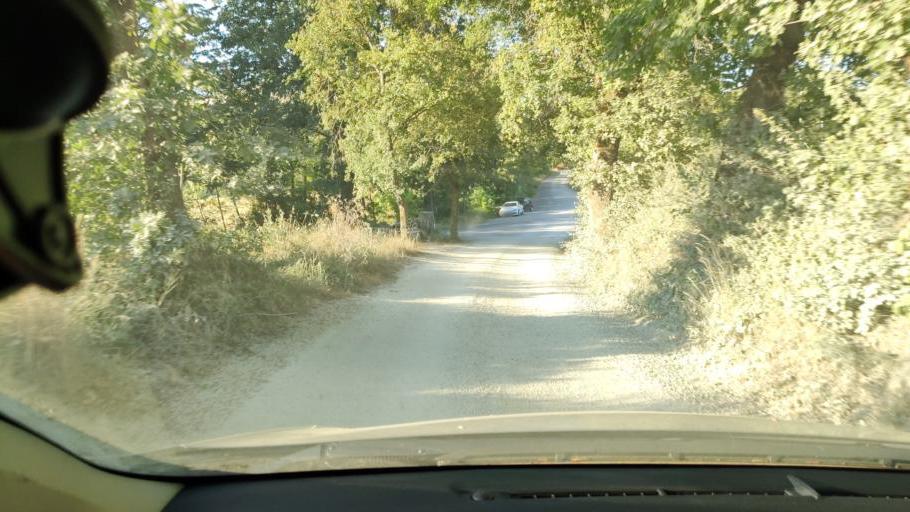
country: IT
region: Umbria
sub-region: Provincia di Terni
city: Amelia
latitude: 42.5491
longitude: 12.4104
